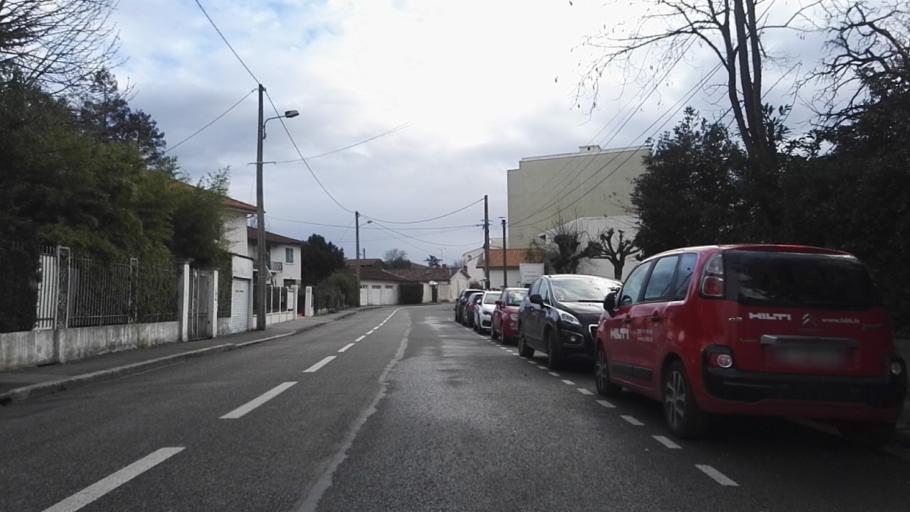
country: FR
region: Aquitaine
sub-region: Departement de la Gironde
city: Bruges
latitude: 44.8583
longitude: -0.6198
